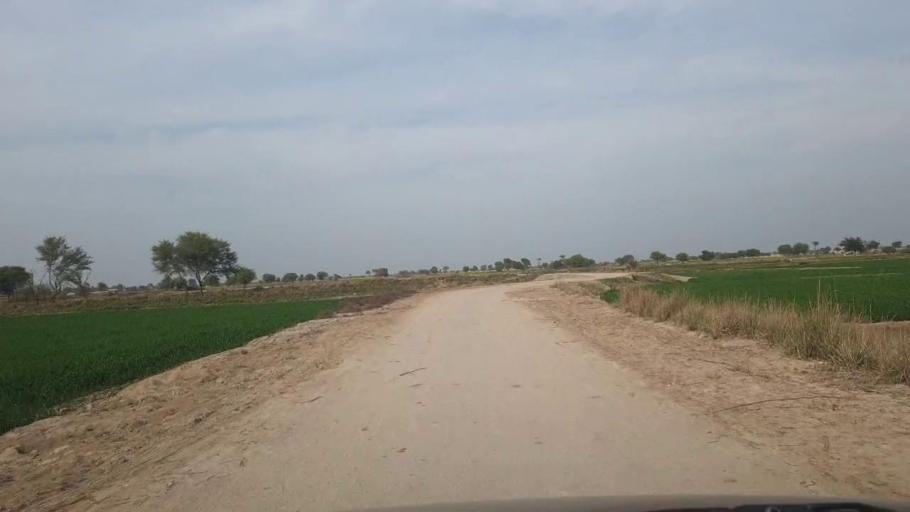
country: PK
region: Sindh
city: Shahpur Chakar
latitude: 26.1127
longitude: 68.5050
